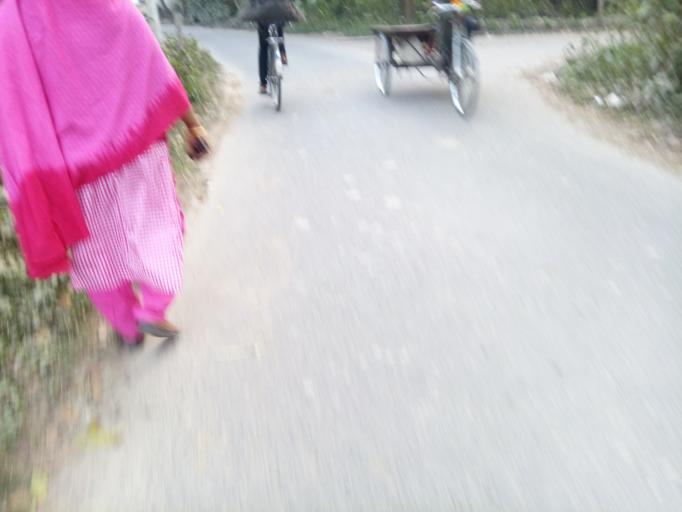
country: BD
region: Khulna
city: Kaliganj
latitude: 23.3557
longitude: 88.9203
